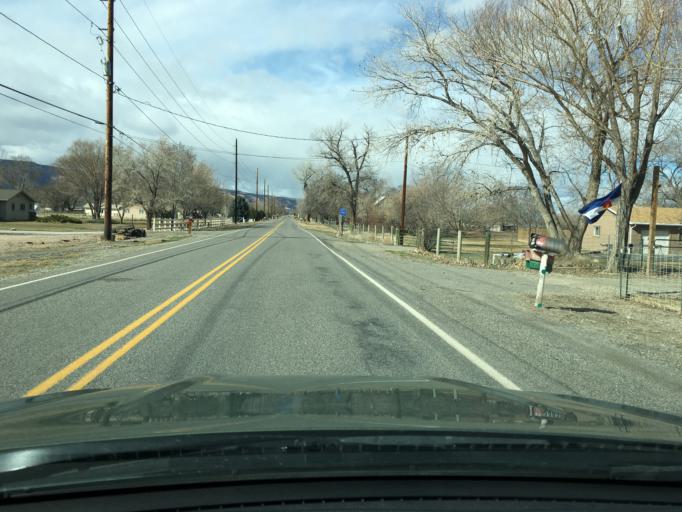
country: US
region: Colorado
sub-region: Mesa County
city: Redlands
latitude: 39.1209
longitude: -108.6095
